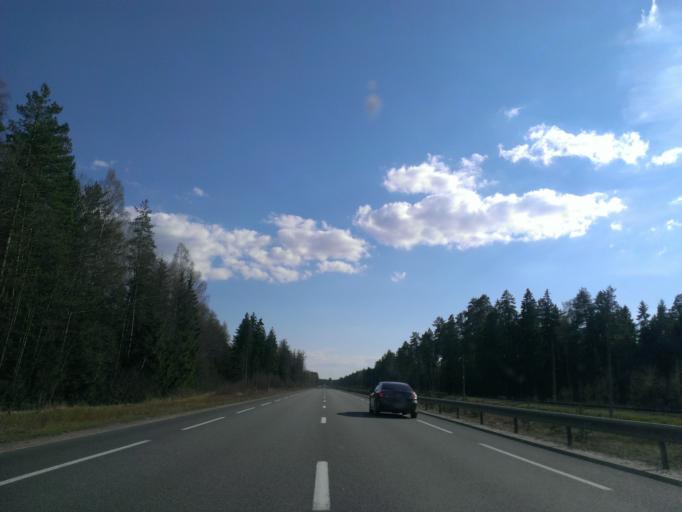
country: LV
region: Saulkrastu
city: Saulkrasti
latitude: 57.3038
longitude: 24.4418
